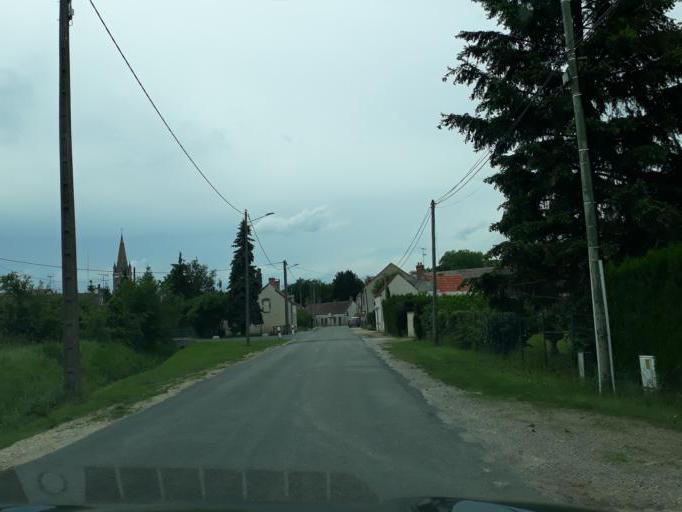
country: FR
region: Centre
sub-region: Departement du Loiret
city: Tigy
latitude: 47.7939
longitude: 2.2035
